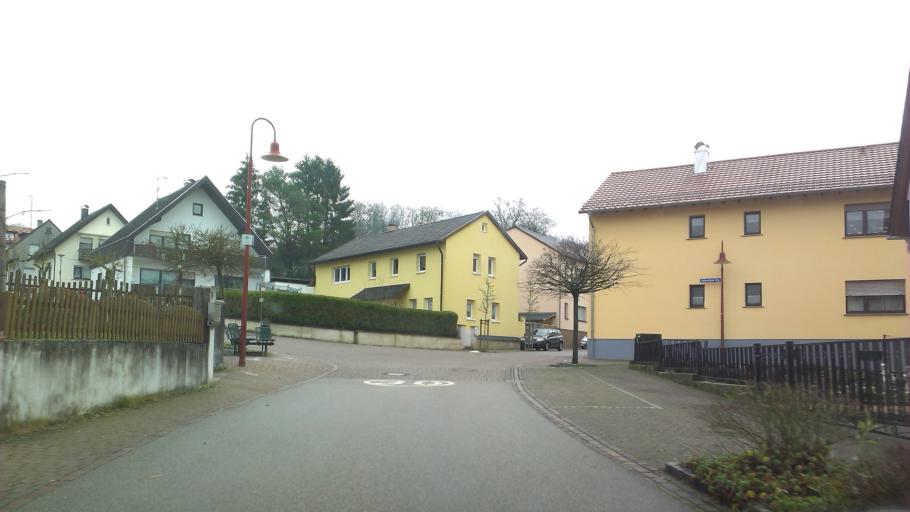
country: DE
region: Baden-Wuerttemberg
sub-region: Karlsruhe Region
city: Horrenberg
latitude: 49.2626
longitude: 8.7600
